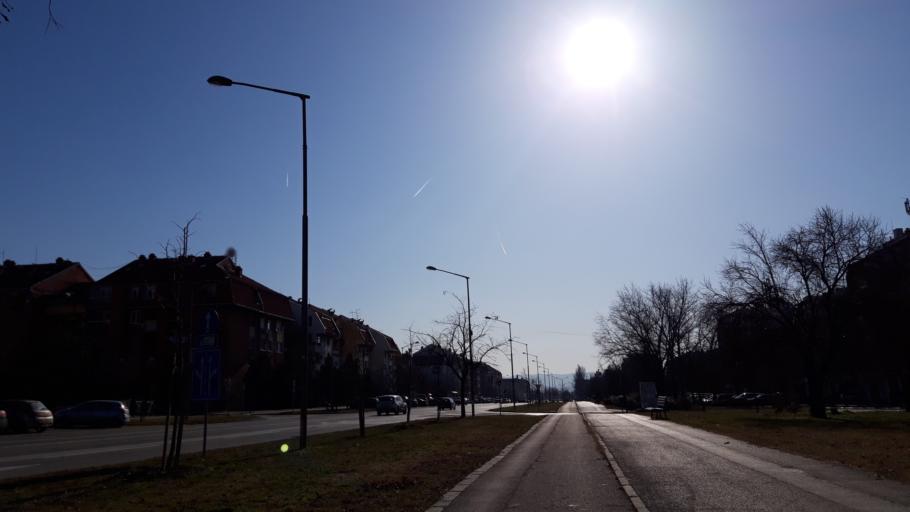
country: RS
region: Autonomna Pokrajina Vojvodina
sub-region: Juznobacki Okrug
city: Novi Sad
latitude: 45.2568
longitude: 19.8016
